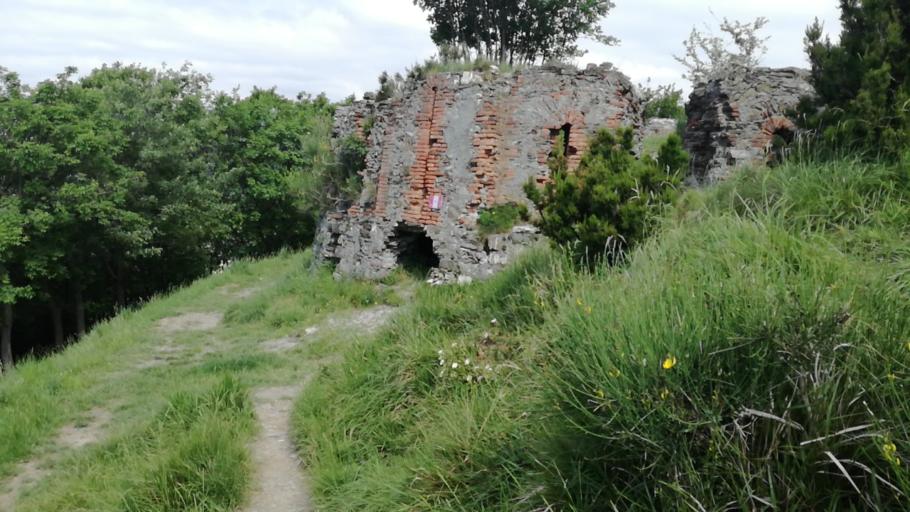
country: IT
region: Liguria
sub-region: Provincia di Genova
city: Genoa
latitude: 44.4290
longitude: 8.9041
